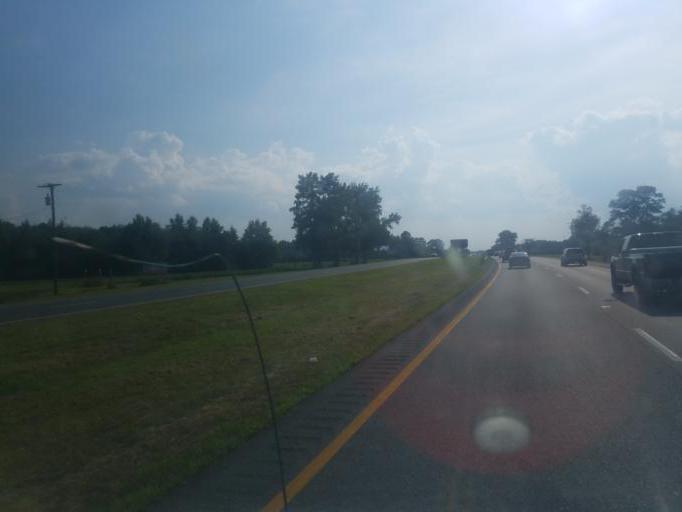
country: US
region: Maryland
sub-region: Worcester County
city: Berlin
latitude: 38.3472
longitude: -75.1775
